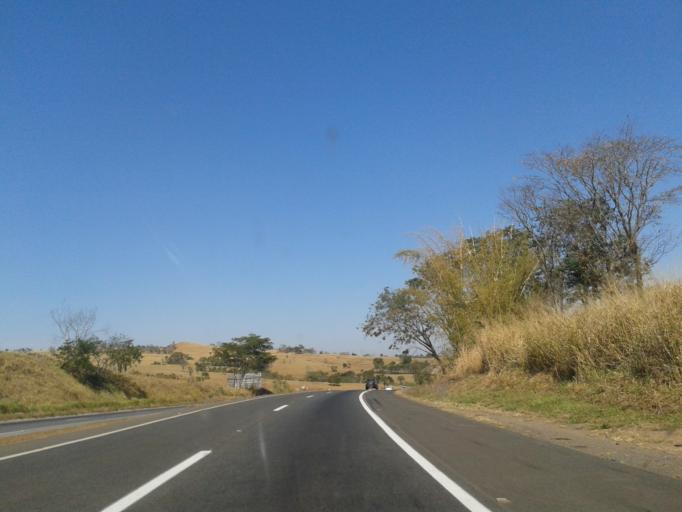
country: BR
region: Goias
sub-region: Piracanjuba
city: Piracanjuba
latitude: -17.2059
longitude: -49.2100
